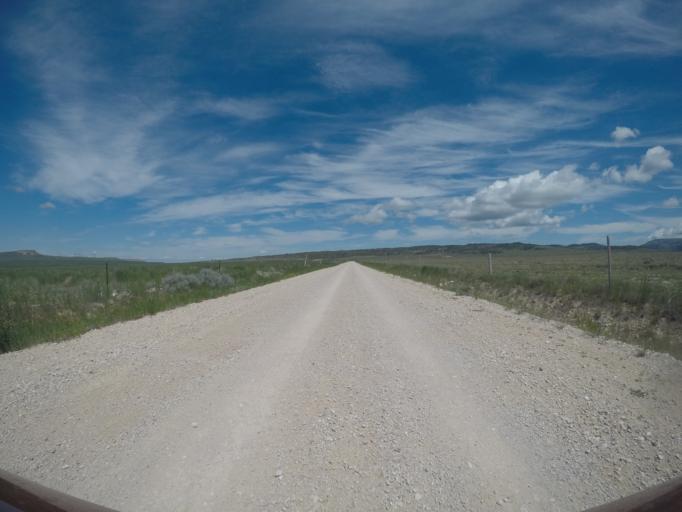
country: US
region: Montana
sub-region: Yellowstone County
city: Laurel
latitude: 45.2287
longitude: -108.6995
